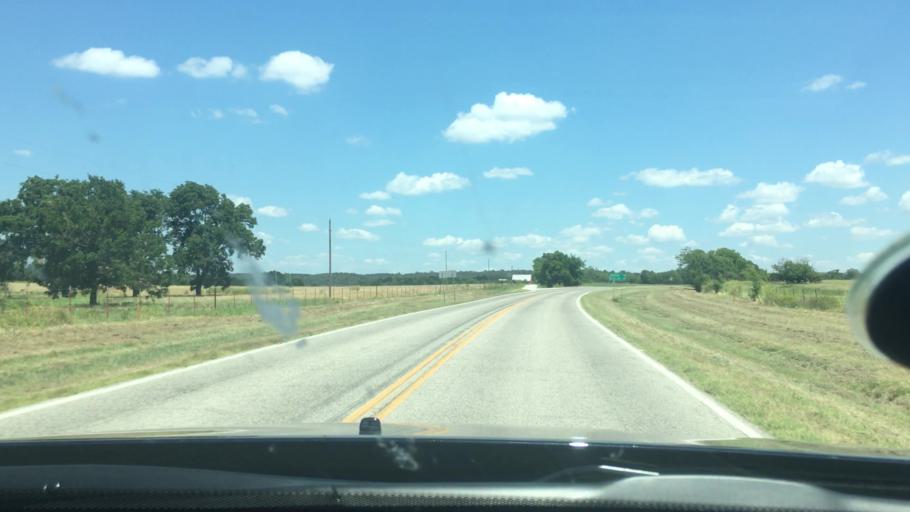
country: US
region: Oklahoma
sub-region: Carter County
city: Dickson
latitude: 34.2900
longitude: -96.9683
